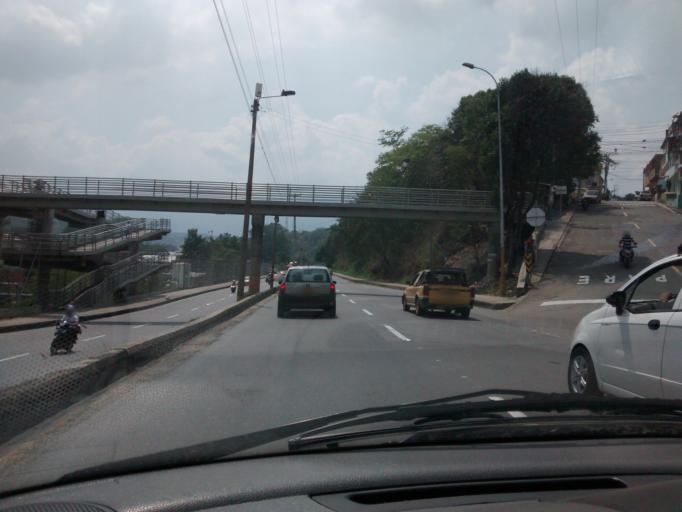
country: CO
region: Santander
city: Bucaramanga
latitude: 7.0925
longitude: -73.1239
